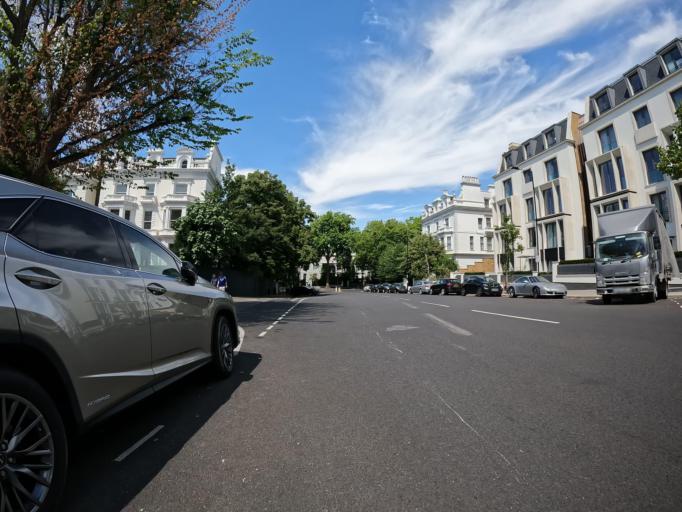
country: GB
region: England
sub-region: Greater London
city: Kensington
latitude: 51.5068
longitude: -0.2040
